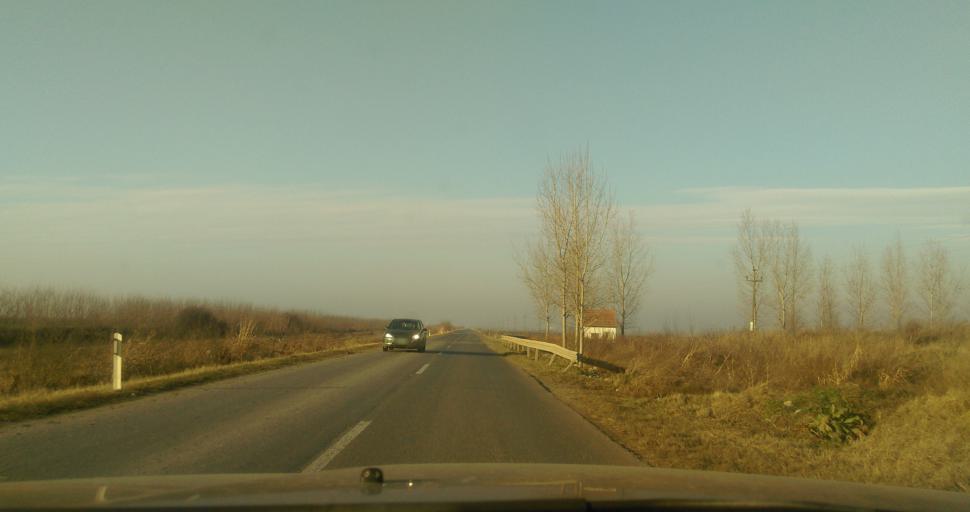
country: RS
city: Curug
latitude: 45.4839
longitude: 20.0394
